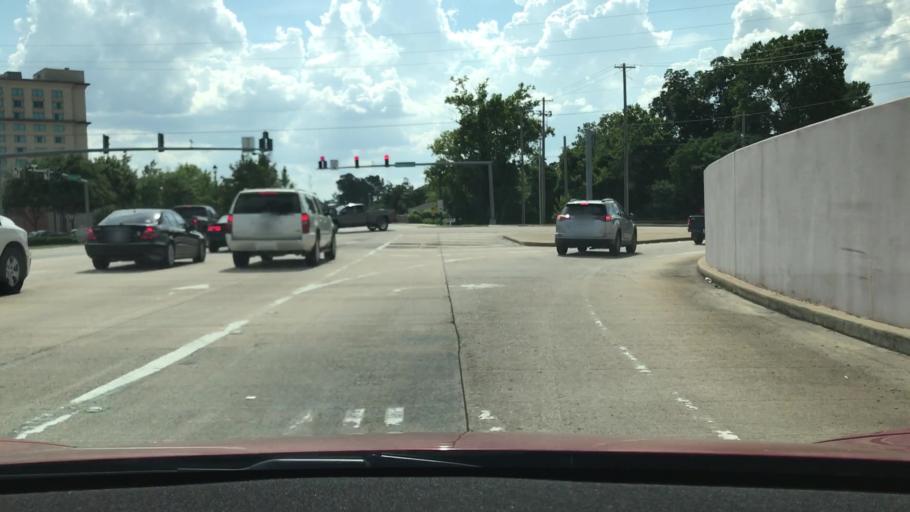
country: US
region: Louisiana
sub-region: Bossier Parish
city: Bossier City
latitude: 32.5120
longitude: -93.7262
